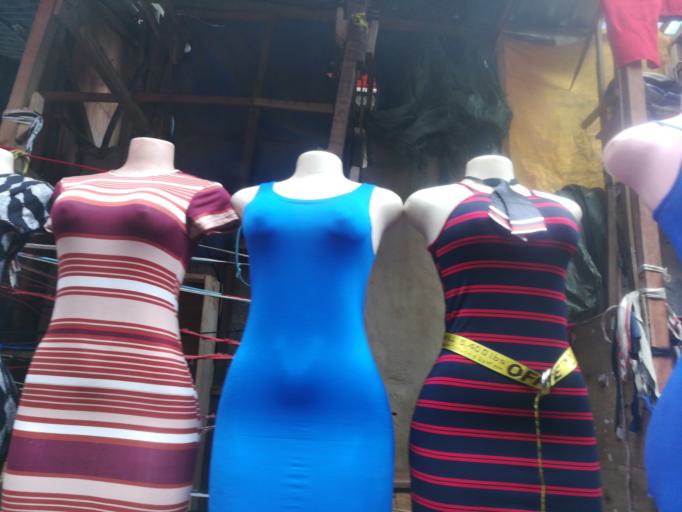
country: NG
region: Lagos
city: Lagos
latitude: 6.4566
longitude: 3.3859
